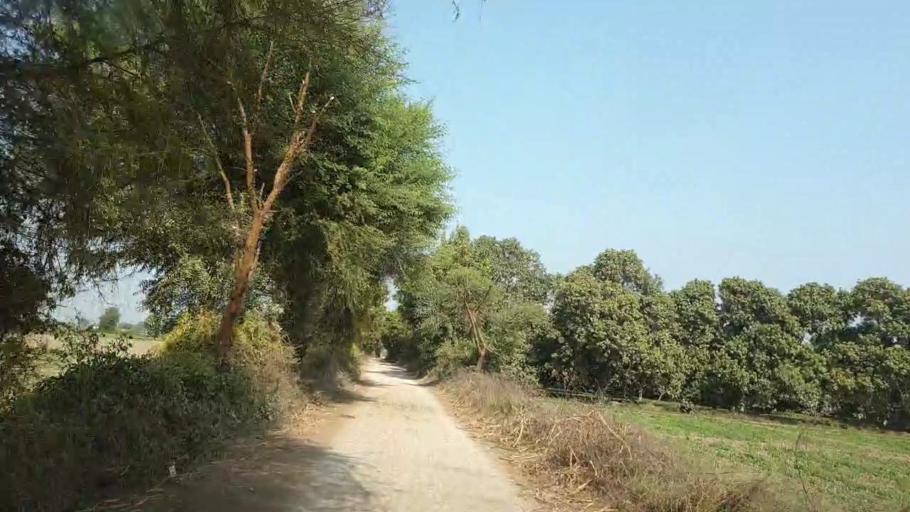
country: PK
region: Sindh
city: Bhit Shah
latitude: 25.7503
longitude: 68.4790
